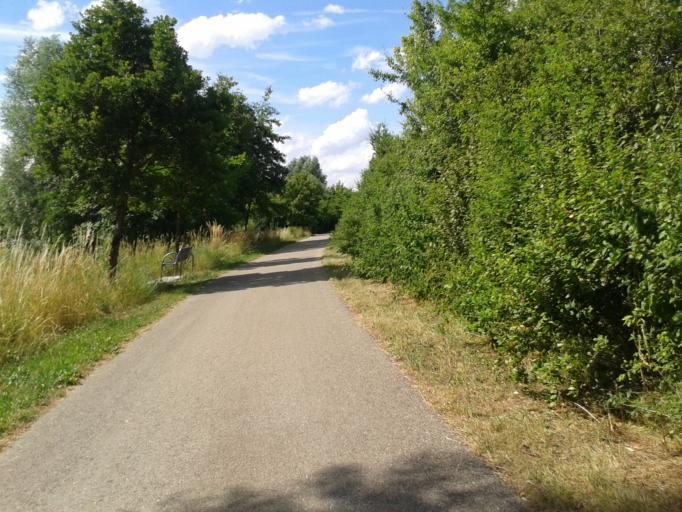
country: DE
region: Baden-Wuerttemberg
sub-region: Regierungsbezirk Stuttgart
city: Aalen
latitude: 48.8354
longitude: 10.0665
